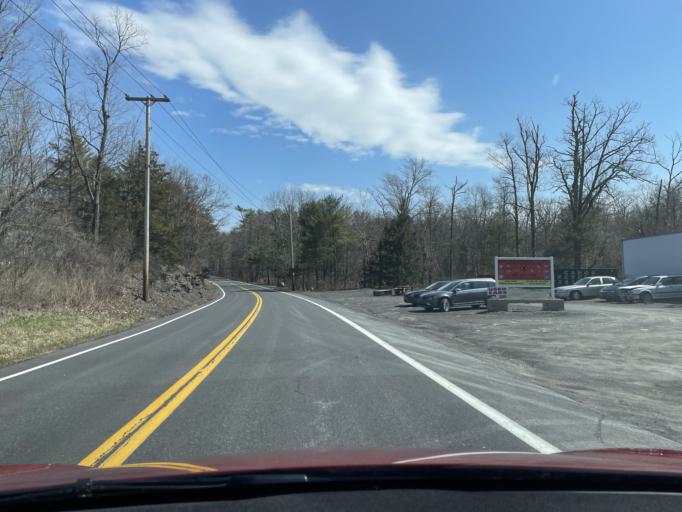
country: US
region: New York
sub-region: Ulster County
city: Manorville
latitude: 42.0730
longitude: -74.0301
